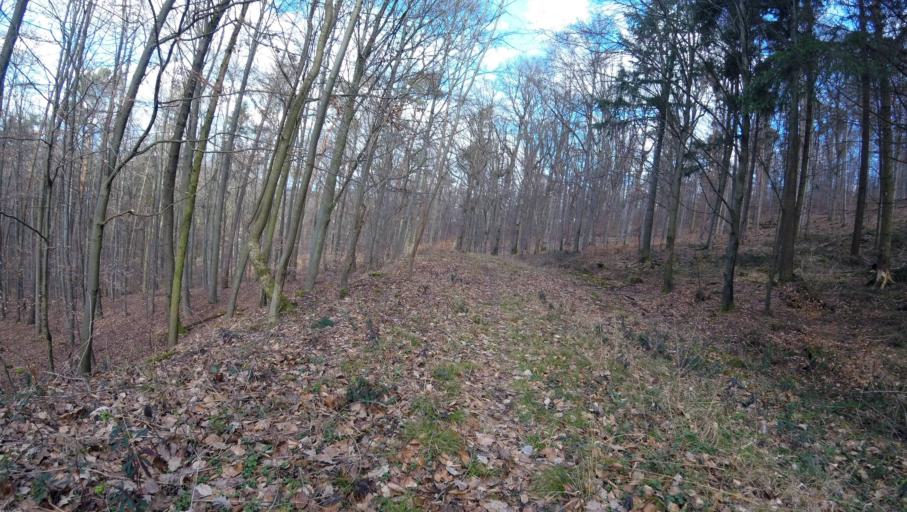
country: DE
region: Baden-Wuerttemberg
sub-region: Regierungsbezirk Stuttgart
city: Grossbottwar
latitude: 48.9979
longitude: 9.3163
